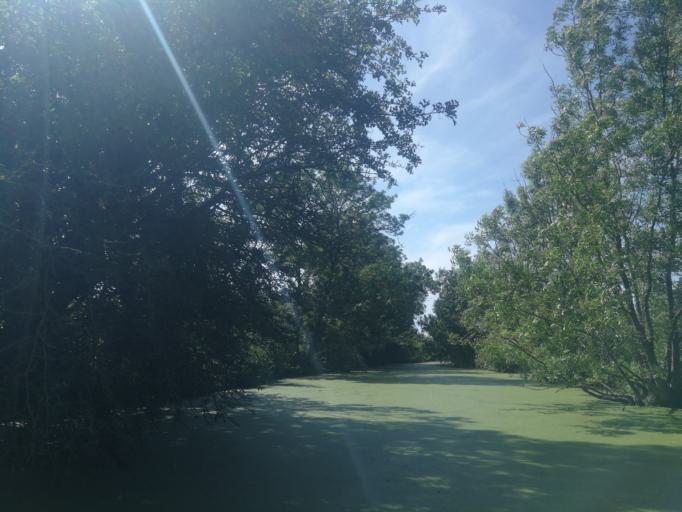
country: FR
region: Poitou-Charentes
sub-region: Departement de la Charente-Maritime
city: Marans
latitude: 46.3616
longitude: -0.9556
